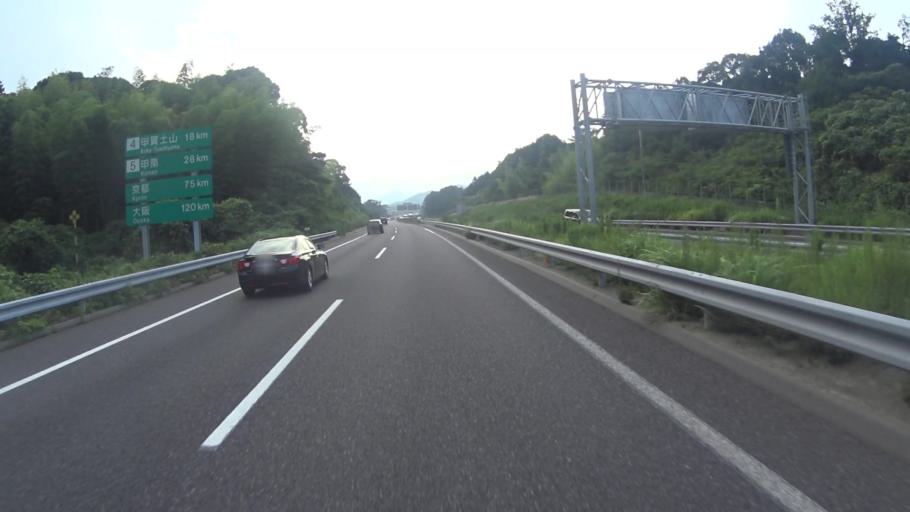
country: JP
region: Mie
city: Kameyama
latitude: 34.8992
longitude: 136.4476
